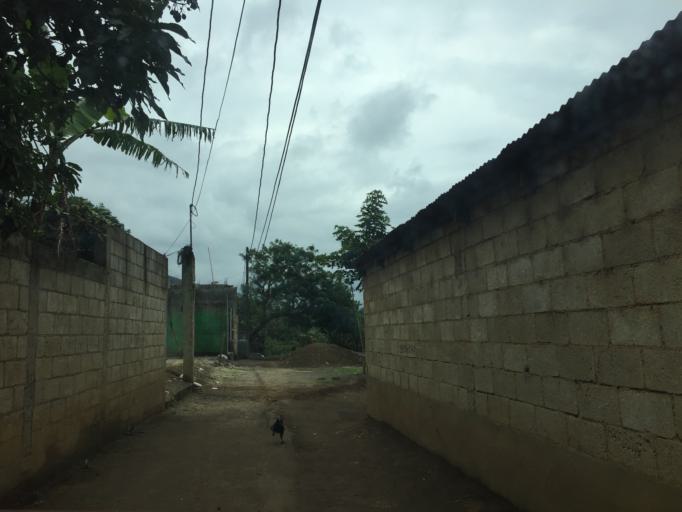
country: GT
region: Guatemala
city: Amatitlan
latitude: 14.5079
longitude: -90.6515
